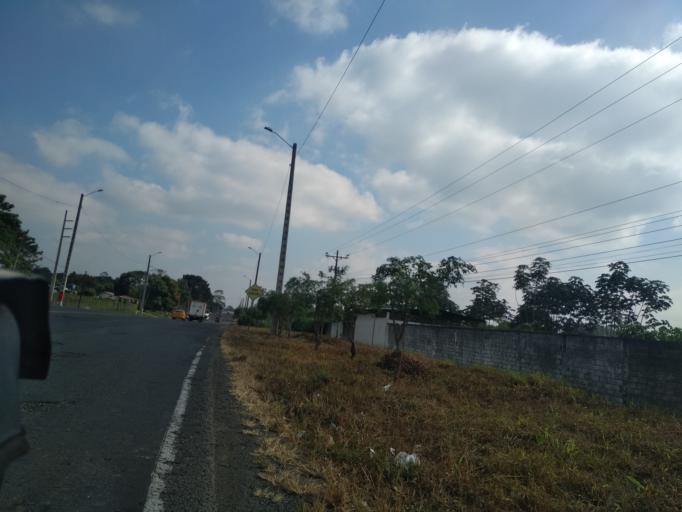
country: EC
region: Los Rios
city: Quevedo
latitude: -1.0710
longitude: -79.4966
